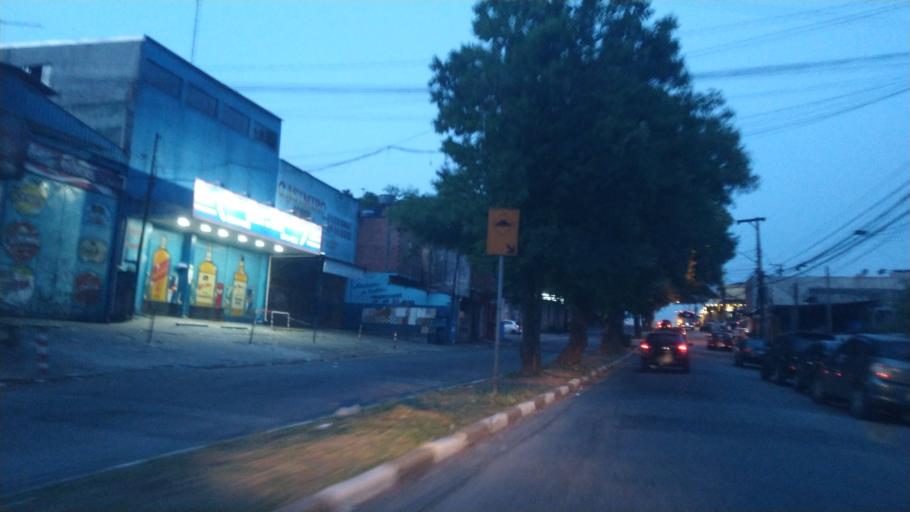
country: BR
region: Sao Paulo
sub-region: Aruja
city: Aruja
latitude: -23.4124
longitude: -46.4041
